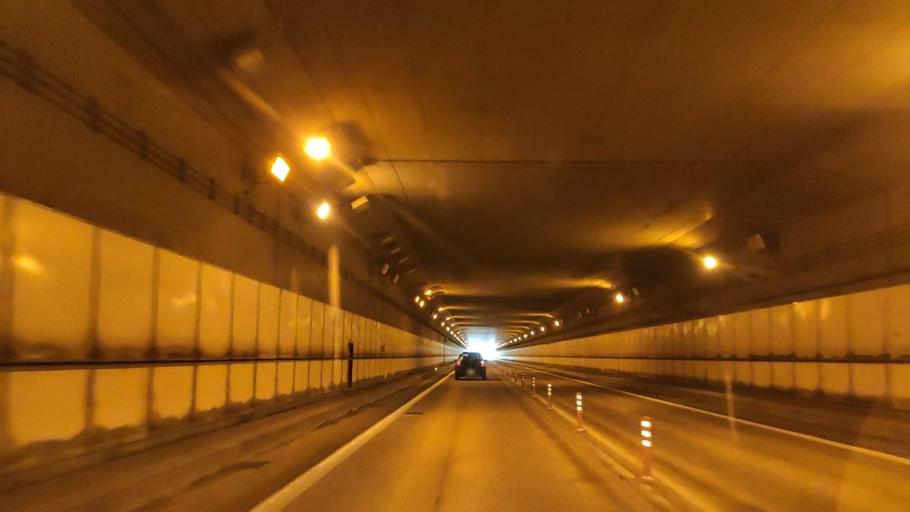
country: JP
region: Akita
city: Odate
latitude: 40.2759
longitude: 140.5346
